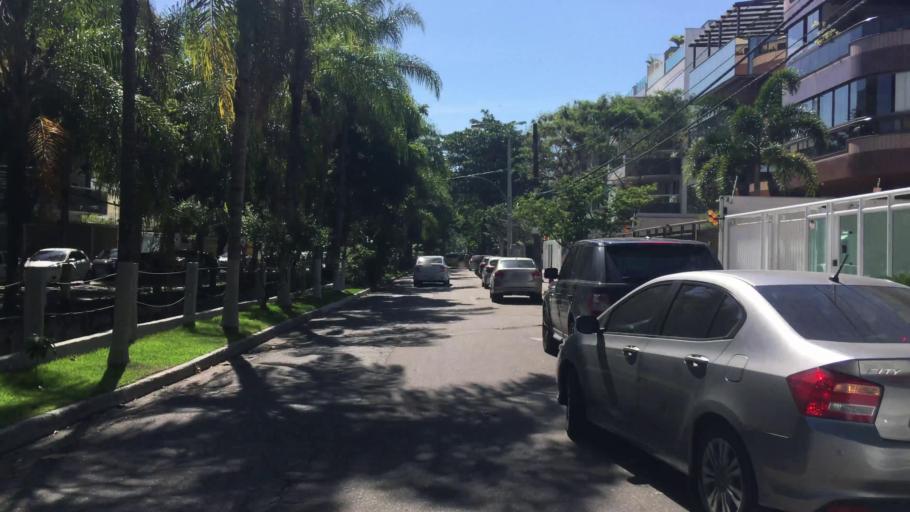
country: BR
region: Rio de Janeiro
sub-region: Rio De Janeiro
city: Rio de Janeiro
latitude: -23.0123
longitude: -43.3027
